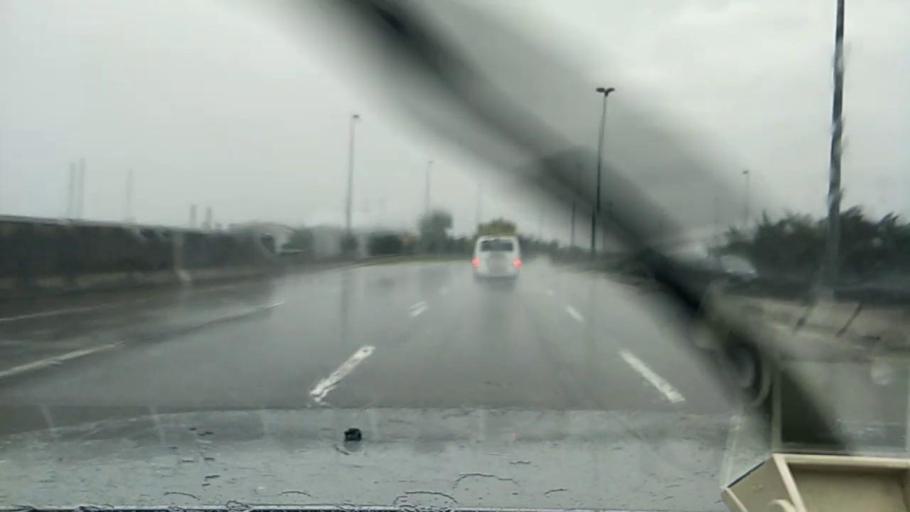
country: MY
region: Selangor
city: Kampong Baharu Balakong
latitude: 2.9956
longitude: 101.7743
